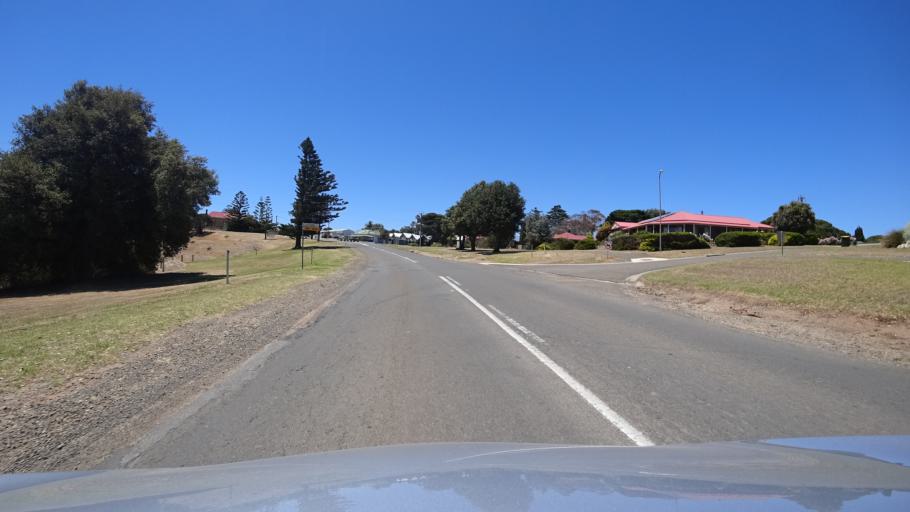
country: AU
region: South Australia
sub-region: Kangaroo Island
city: Kingscote
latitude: -35.7191
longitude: 137.9359
